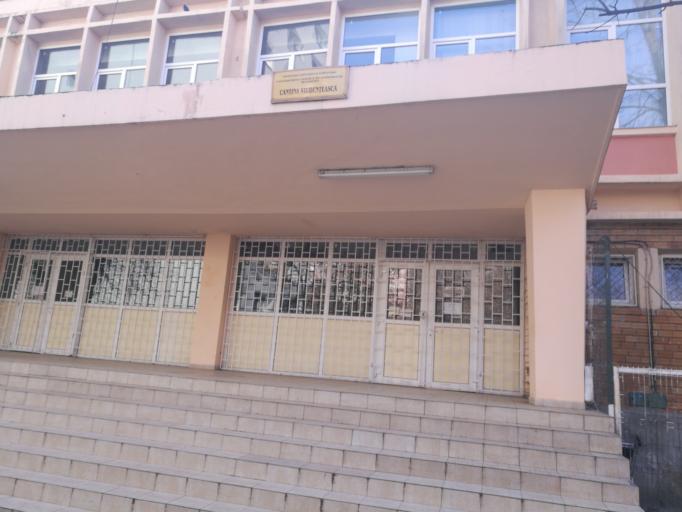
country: RO
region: Bucuresti
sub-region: Municipiul Bucuresti
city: Bucharest
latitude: 44.4620
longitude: 26.1205
